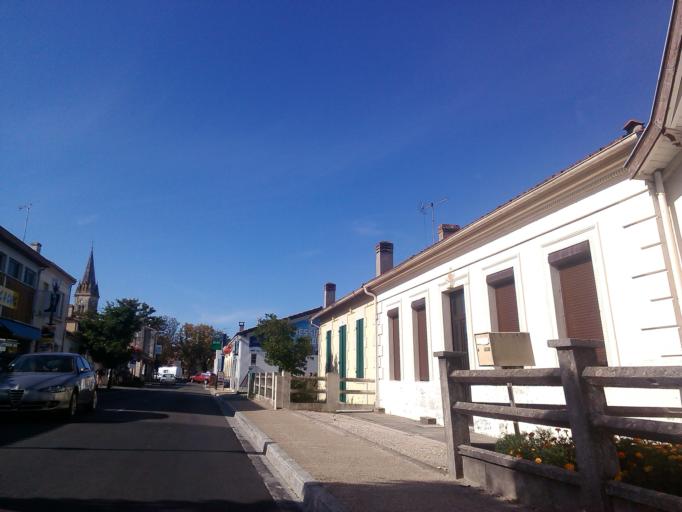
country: FR
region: Aquitaine
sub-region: Departement de la Gironde
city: Hourtin
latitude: 45.1845
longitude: -1.0569
